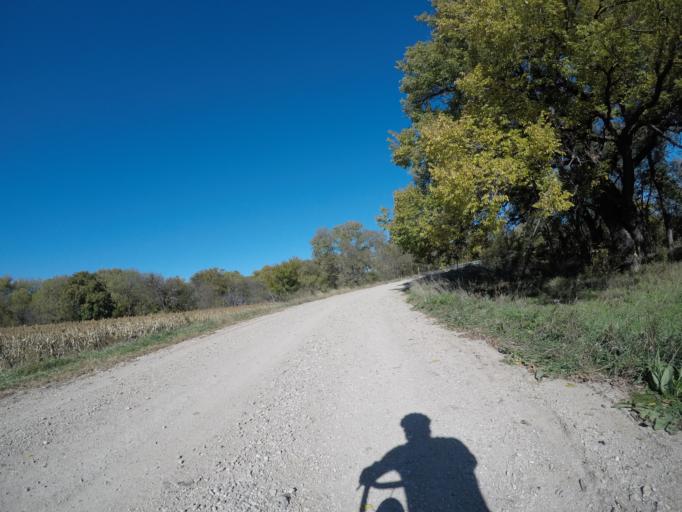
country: US
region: Kansas
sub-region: Wabaunsee County
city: Alma
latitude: 38.9425
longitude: -96.4041
